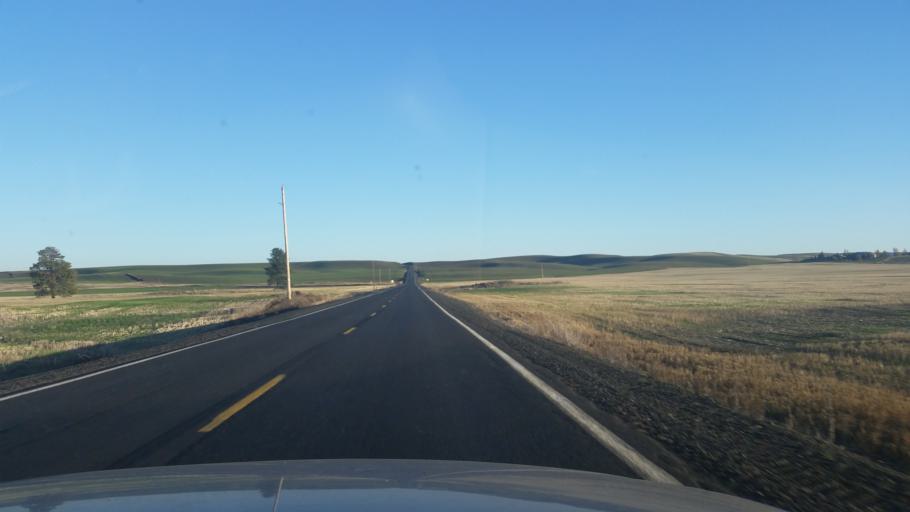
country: US
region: Washington
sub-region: Spokane County
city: Opportunity
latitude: 47.3646
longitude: -117.2866
